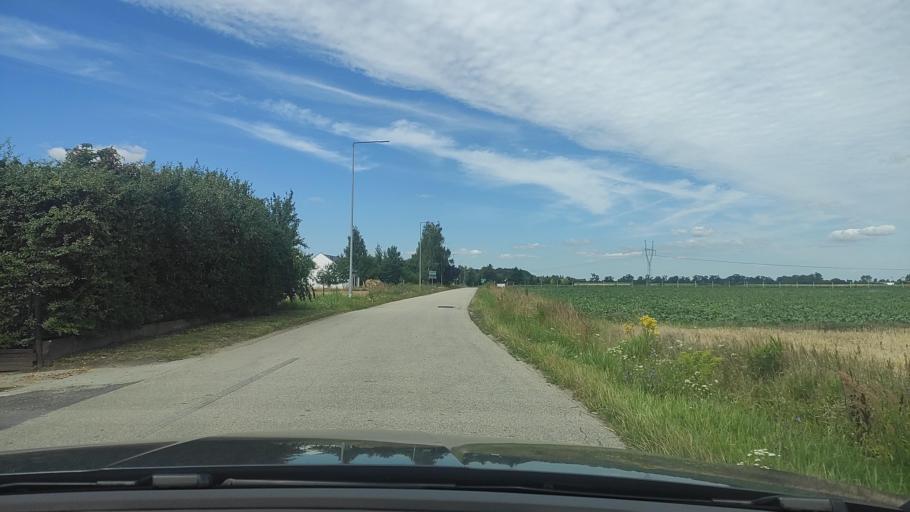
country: PL
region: Greater Poland Voivodeship
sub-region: Powiat poznanski
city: Kostrzyn
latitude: 52.4057
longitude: 17.2204
